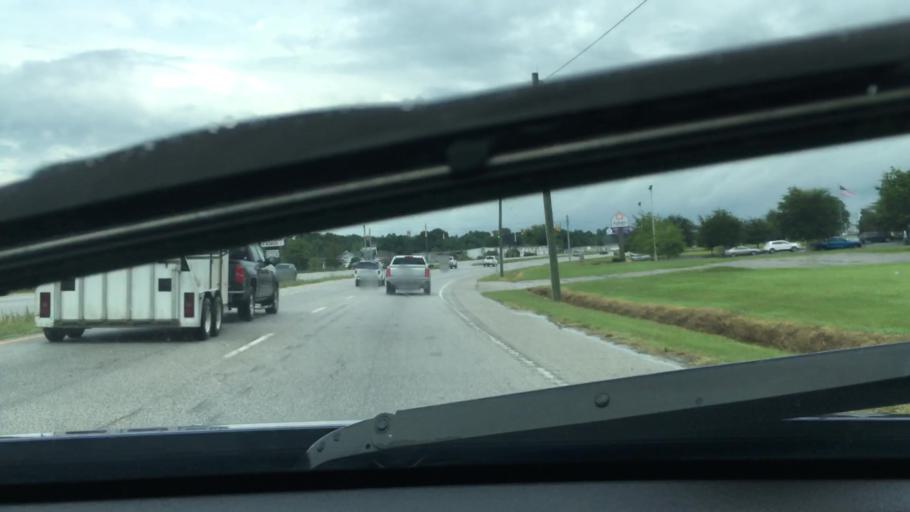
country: US
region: South Carolina
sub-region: Sumter County
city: Cherryvale
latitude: 33.9649
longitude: -80.4086
